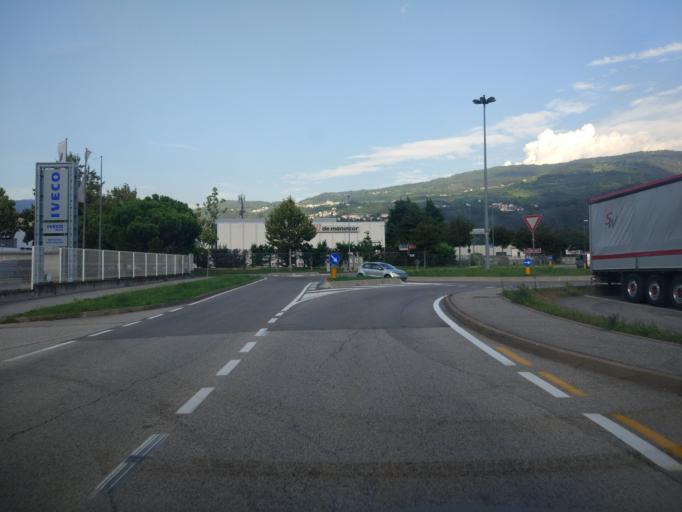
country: IT
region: Trentino-Alto Adige
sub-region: Provincia di Trento
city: Meano
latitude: 46.1186
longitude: 11.0965
